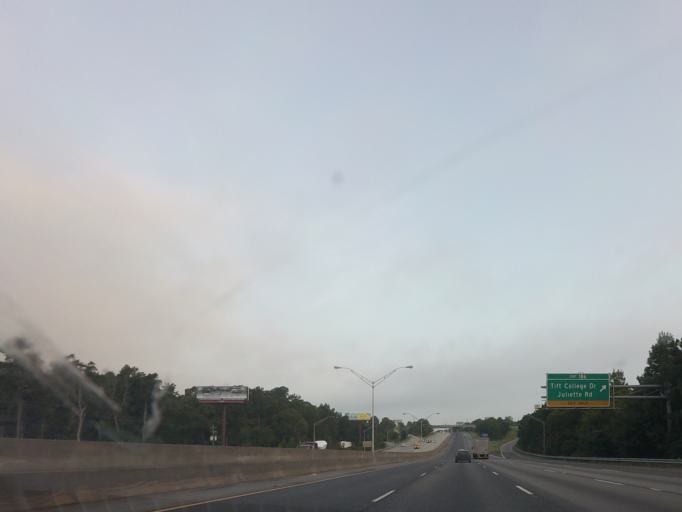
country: US
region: Georgia
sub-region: Monroe County
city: Forsyth
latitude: 33.0318
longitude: -83.9160
